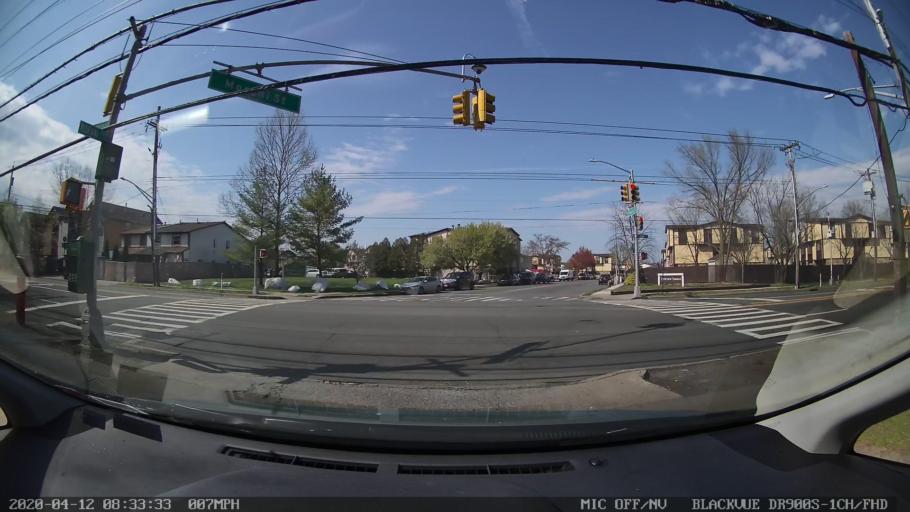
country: US
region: New York
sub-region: Richmond County
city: Bloomfield
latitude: 40.6079
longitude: -74.1573
